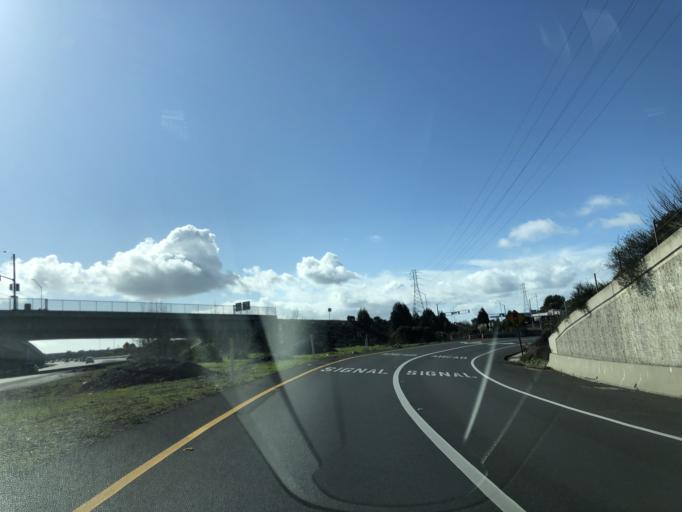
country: US
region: California
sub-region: Contra Costa County
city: Tara Hills
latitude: 37.9880
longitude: -122.3143
